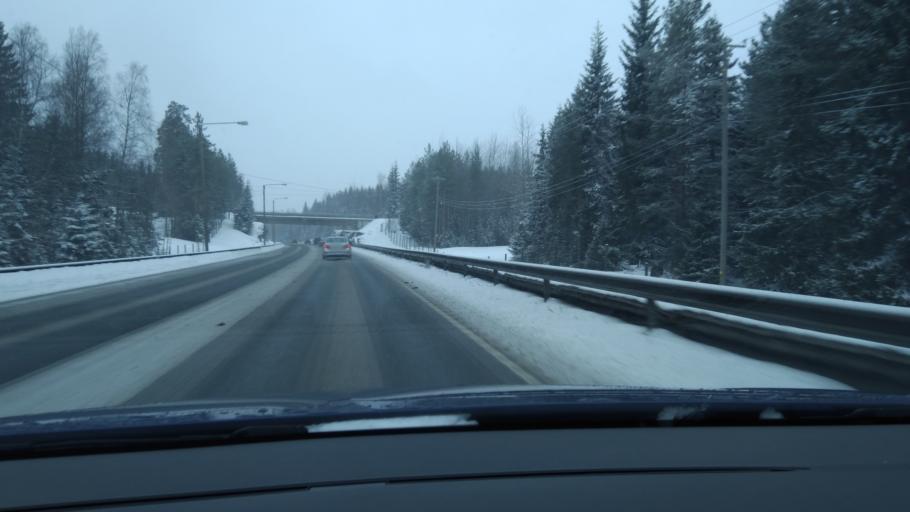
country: FI
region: Pirkanmaa
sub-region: Tampere
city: Kangasala
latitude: 61.5366
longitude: 23.9632
